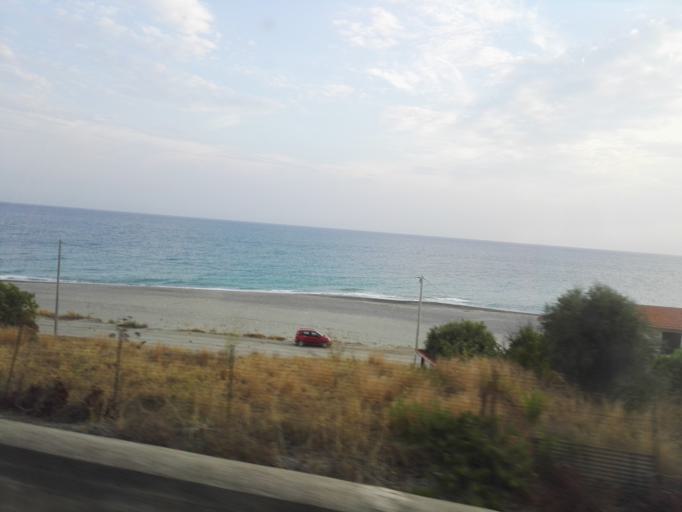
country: IT
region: Calabria
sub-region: Provincia di Reggio Calabria
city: Bova Marina
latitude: 37.9256
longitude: 15.9376
